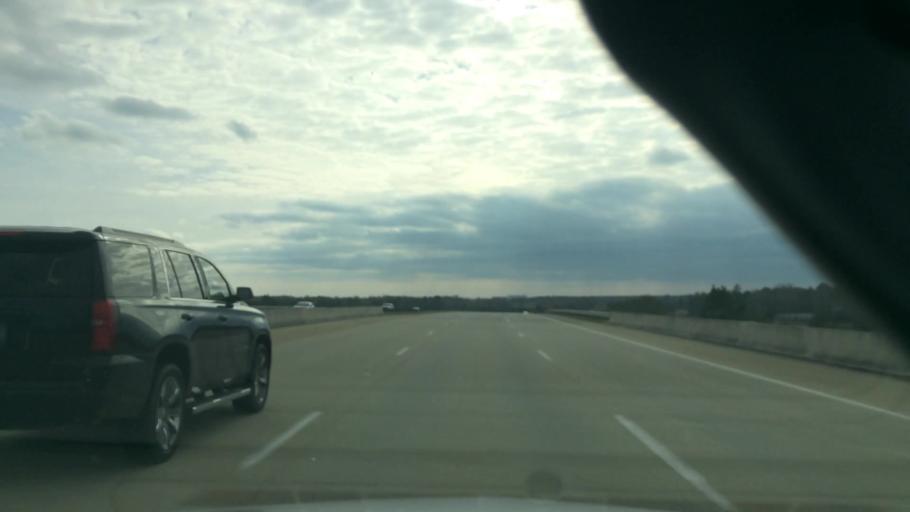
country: US
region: South Carolina
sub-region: Horry County
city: North Myrtle Beach
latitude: 33.8446
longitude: -78.7013
